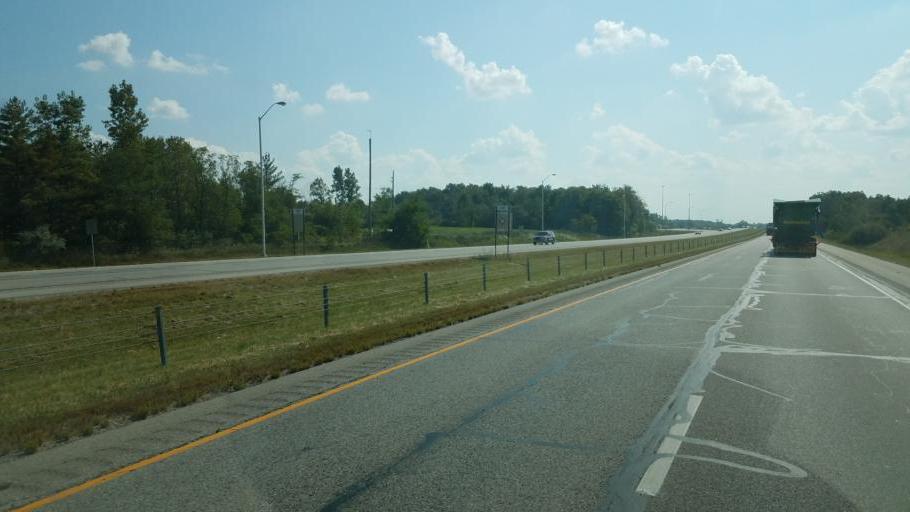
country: US
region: Indiana
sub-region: DeKalb County
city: Garrett
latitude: 41.3025
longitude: -85.0877
